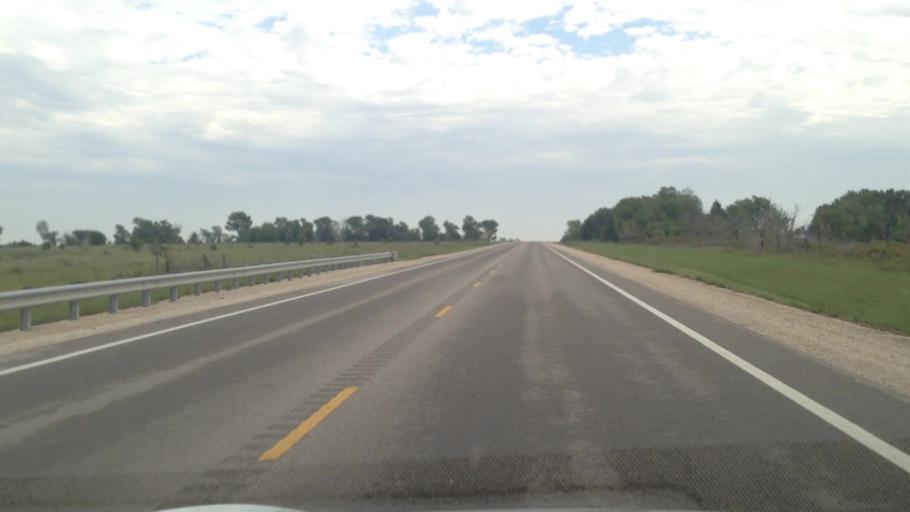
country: US
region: Kansas
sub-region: Allen County
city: Iola
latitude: 37.9092
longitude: -95.1123
